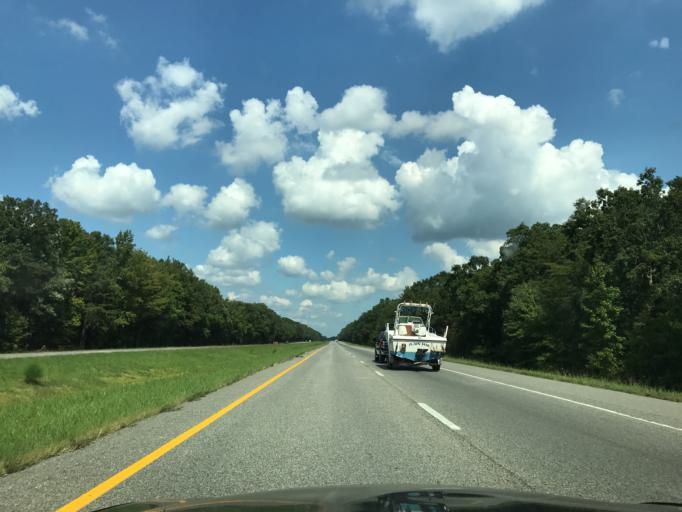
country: US
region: Delaware
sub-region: New Castle County
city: Townsend
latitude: 39.3291
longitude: -75.8419
